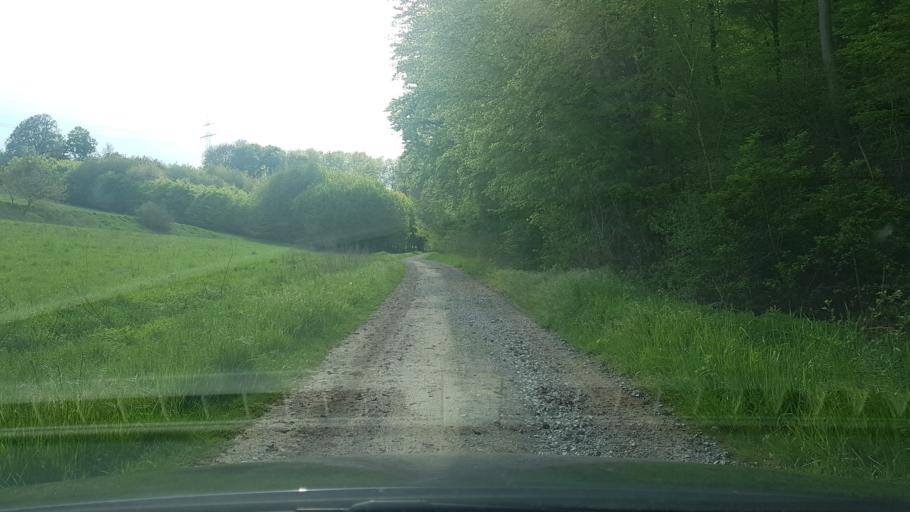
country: DE
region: North Rhine-Westphalia
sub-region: Regierungsbezirk Detmold
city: Paderborn
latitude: 51.6541
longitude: 8.7705
